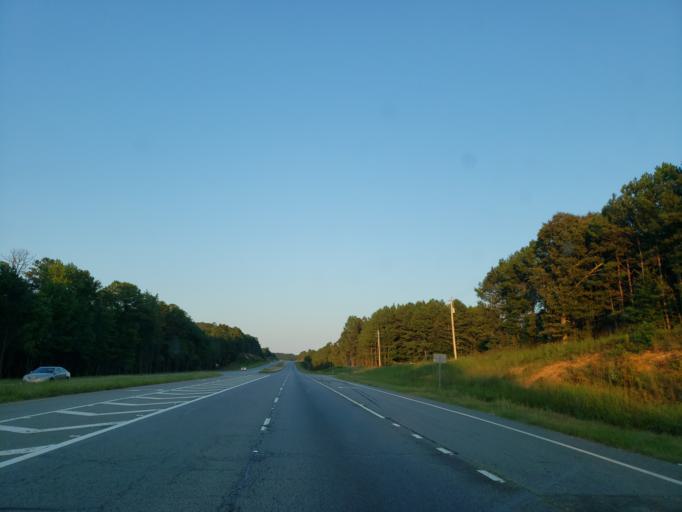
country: US
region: Georgia
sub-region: Bartow County
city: Euharlee
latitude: 34.2198
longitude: -84.9184
